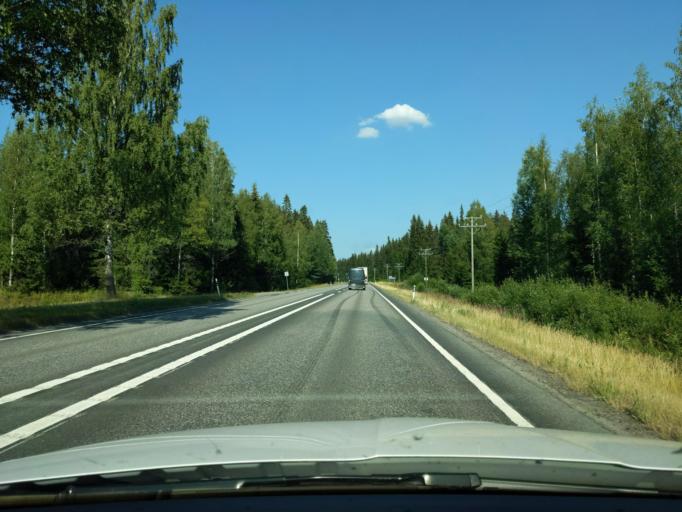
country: FI
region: Paijanne Tavastia
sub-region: Lahti
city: Hollola
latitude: 60.9389
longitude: 25.3973
